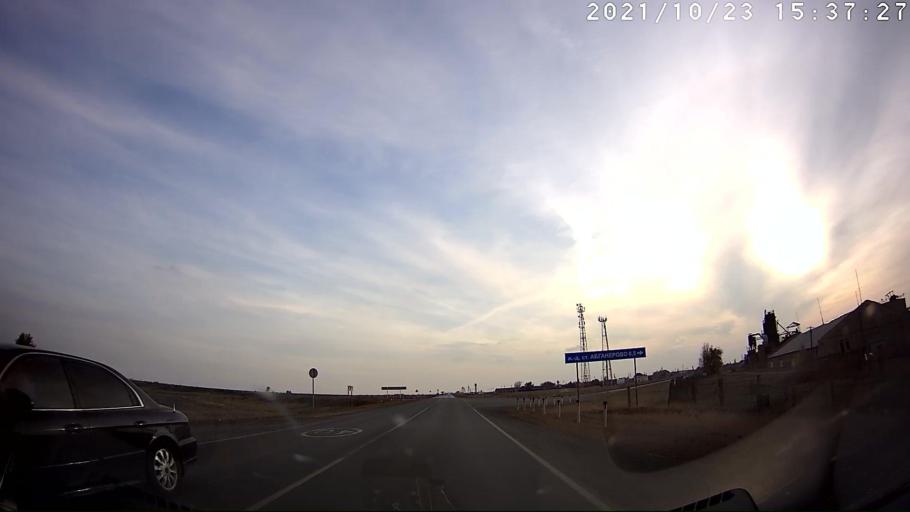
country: RU
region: Volgograd
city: Bereslavka
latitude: 48.1441
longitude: 44.1232
